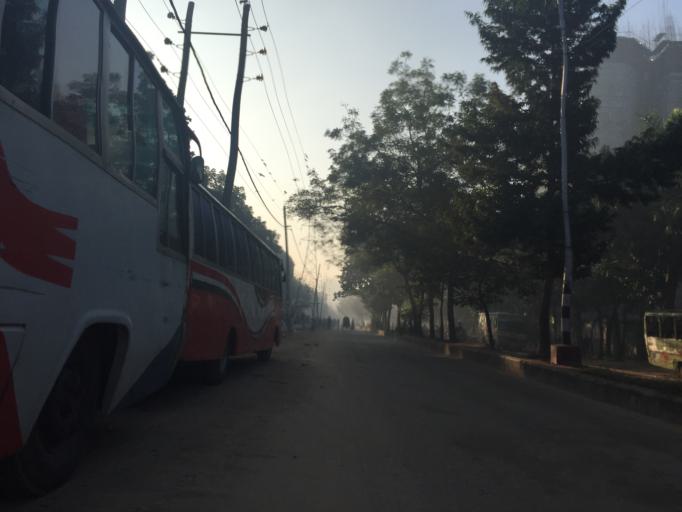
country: BD
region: Dhaka
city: Azimpur
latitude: 23.8093
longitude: 90.3504
